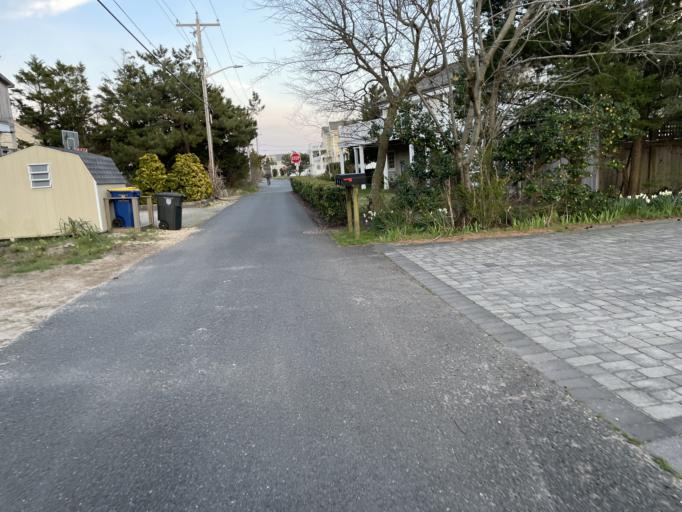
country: US
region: Delaware
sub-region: Sussex County
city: Lewes
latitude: 38.7823
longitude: -75.1393
